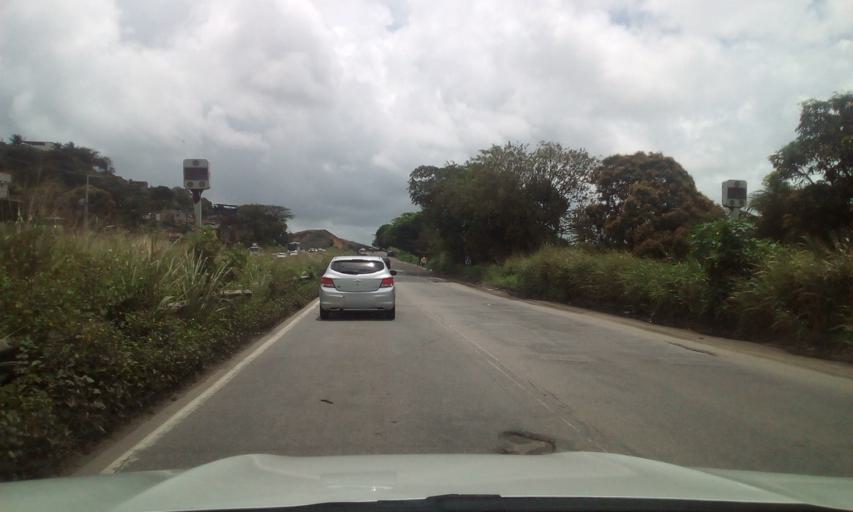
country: BR
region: Pernambuco
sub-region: Jaboatao Dos Guararapes
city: Jaboatao dos Guararapes
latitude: -8.1127
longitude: -34.9455
